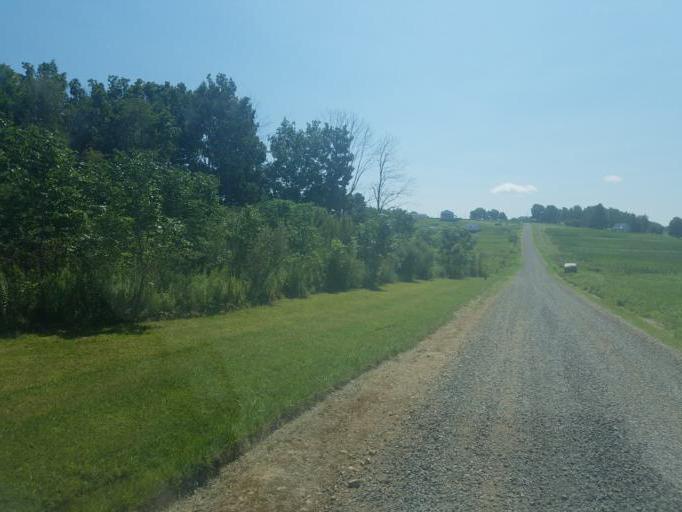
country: US
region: Pennsylvania
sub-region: Clarion County
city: Knox
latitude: 41.2002
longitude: -79.5498
